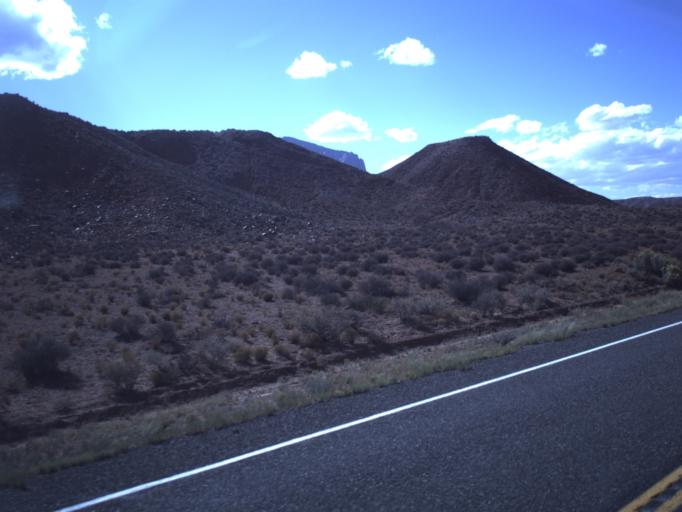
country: US
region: Utah
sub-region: Wayne County
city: Loa
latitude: 38.1467
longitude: -110.6159
